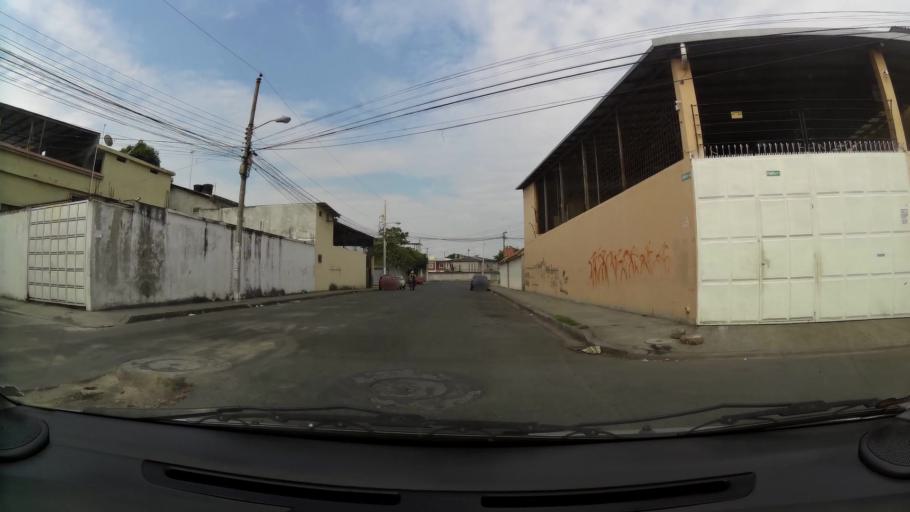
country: EC
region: Guayas
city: Guayaquil
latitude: -2.2608
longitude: -79.8981
